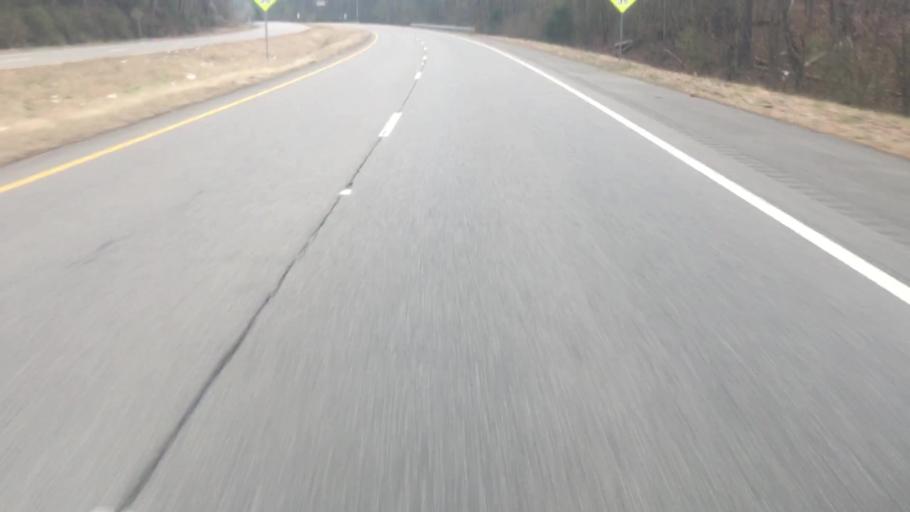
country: US
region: Alabama
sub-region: Walker County
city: Cordova
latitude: 33.8219
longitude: -87.1879
